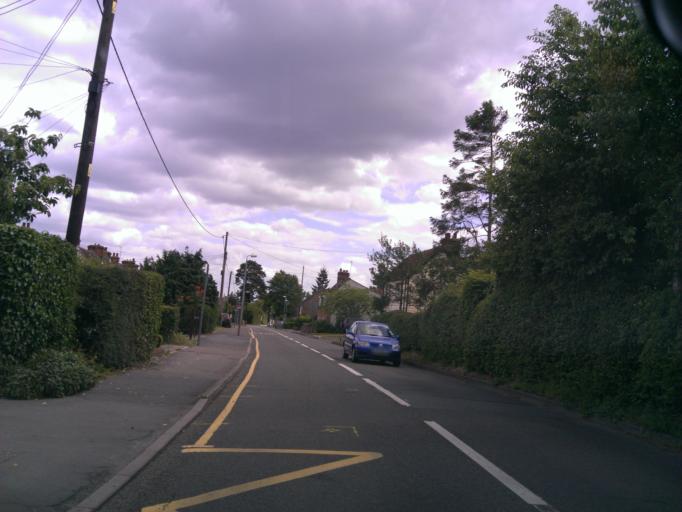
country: GB
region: England
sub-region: Essex
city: Witham
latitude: 51.8279
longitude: 0.6512
